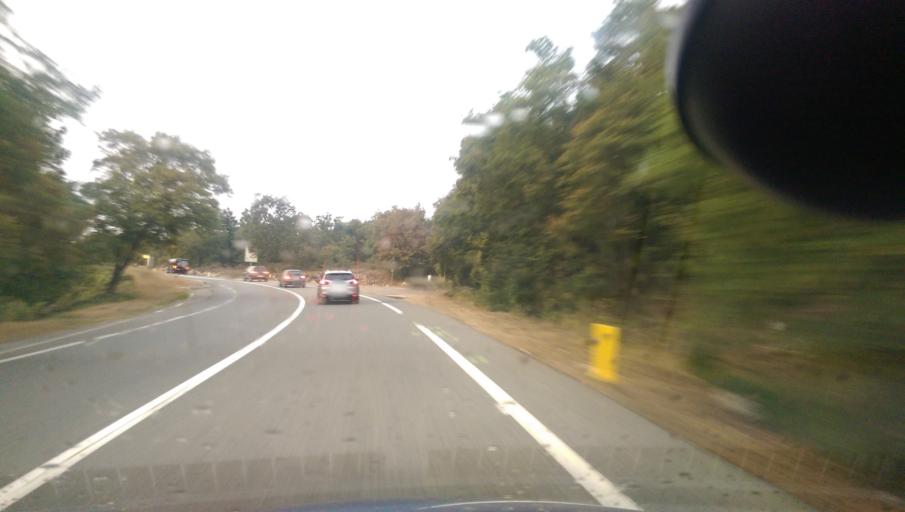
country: FR
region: Provence-Alpes-Cote d'Azur
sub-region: Departement des Alpes-Maritimes
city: Cabris
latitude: 43.6846
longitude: 6.8849
